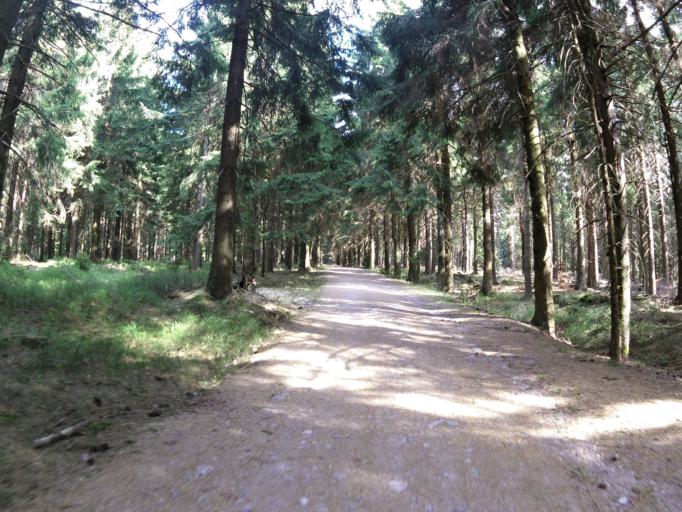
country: DE
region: Thuringia
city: Oberhof
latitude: 50.7036
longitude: 10.7019
